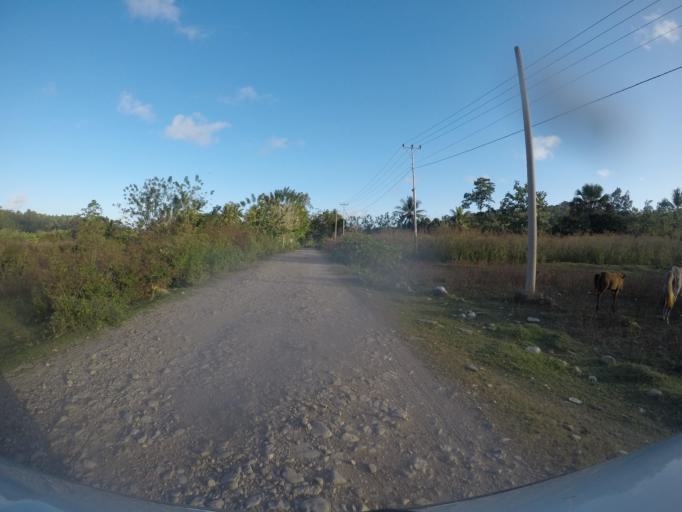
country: TL
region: Baucau
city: Venilale
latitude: -8.7296
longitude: 126.7090
